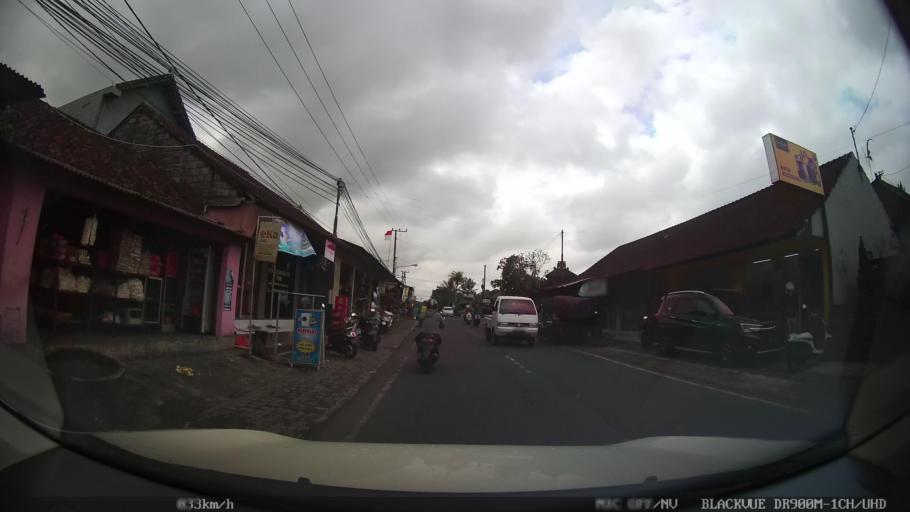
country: ID
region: Bali
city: Banjar Mambalkajanan
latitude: -8.5506
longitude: 115.2265
